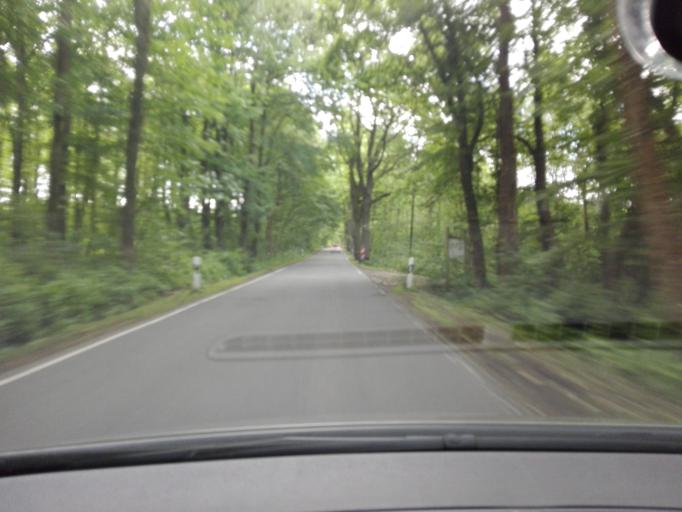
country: DE
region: North Rhine-Westphalia
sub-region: Regierungsbezirk Arnsberg
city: Frondenberg
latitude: 51.4948
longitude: 7.7519
